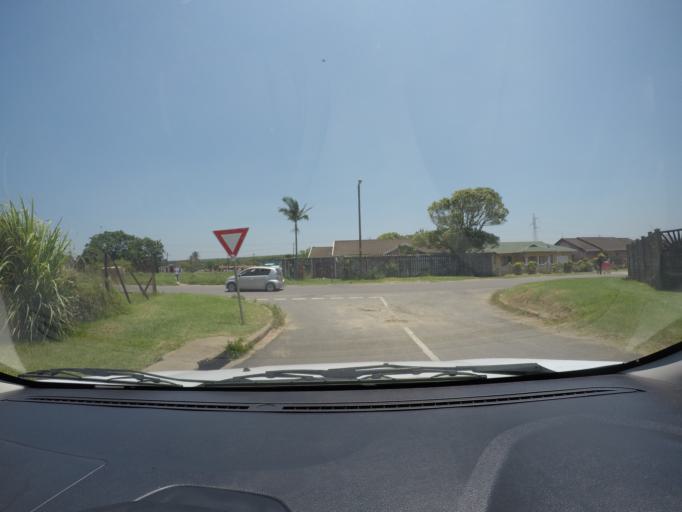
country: ZA
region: KwaZulu-Natal
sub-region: uThungulu District Municipality
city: eSikhawini
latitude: -28.8751
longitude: 31.8969
